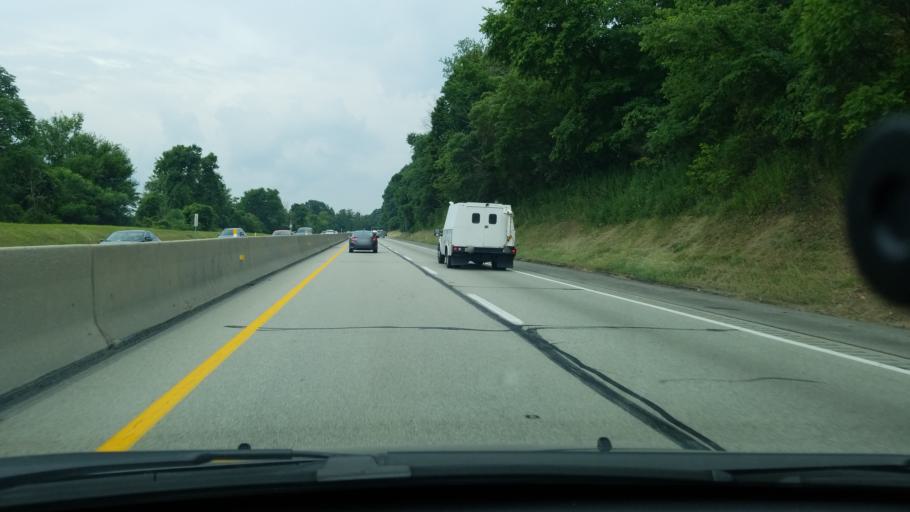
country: US
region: Pennsylvania
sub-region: Allegheny County
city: Plum
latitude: 40.4858
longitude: -79.7767
